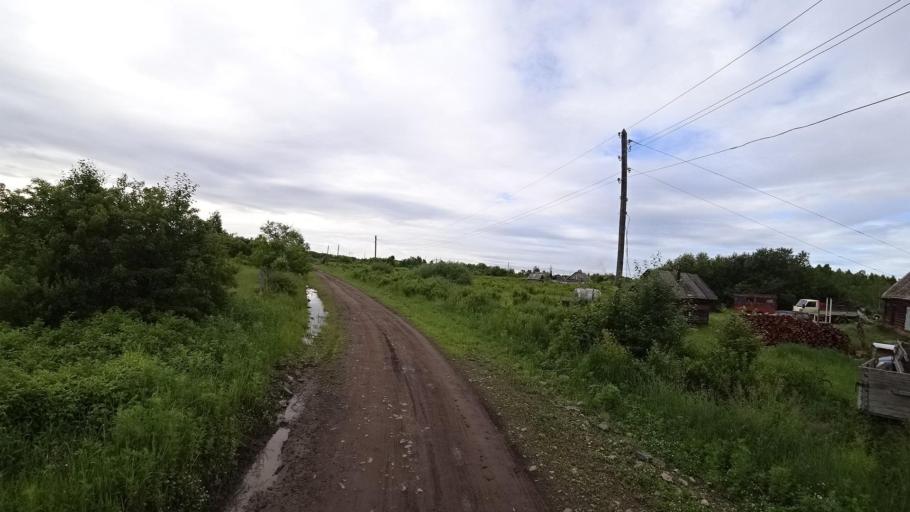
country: RU
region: Khabarovsk Krai
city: Amursk
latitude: 49.8856
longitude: 136.1278
